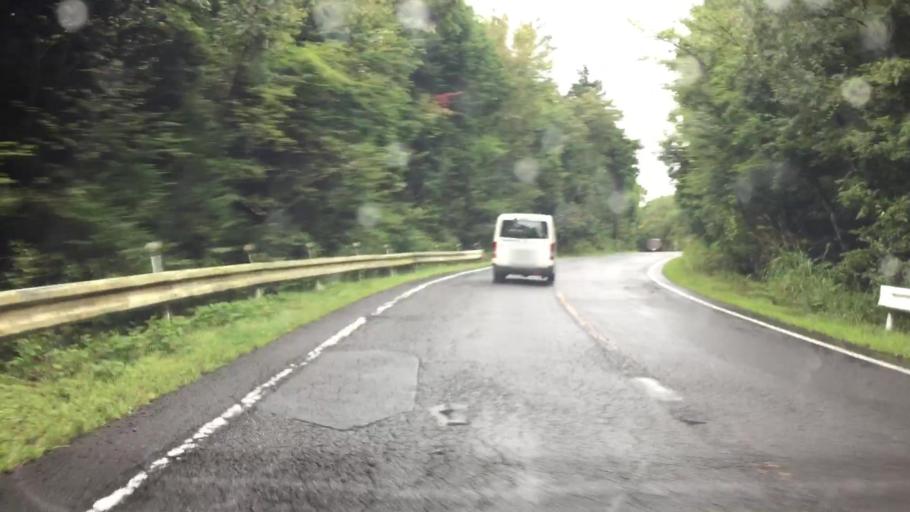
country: JP
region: Yamanashi
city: Fujikawaguchiko
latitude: 35.4680
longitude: 138.6663
